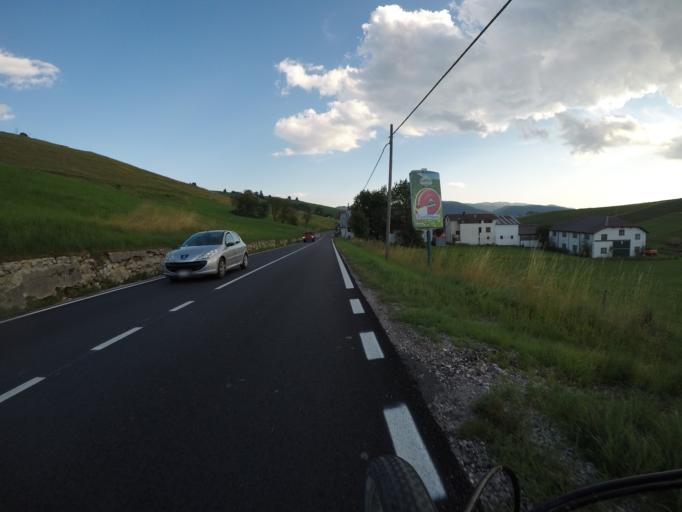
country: IT
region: Veneto
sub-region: Provincia di Vicenza
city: Gallio
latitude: 45.8811
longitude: 11.5483
